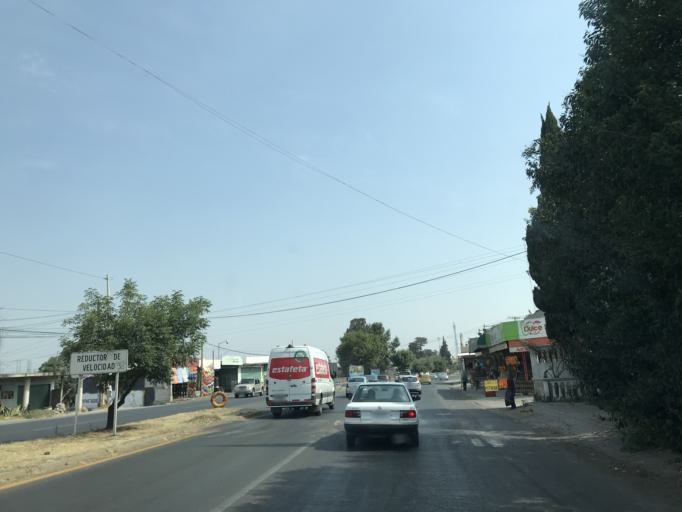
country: MX
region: Tlaxcala
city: Xiloxoxtla
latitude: 19.2585
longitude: -98.2004
